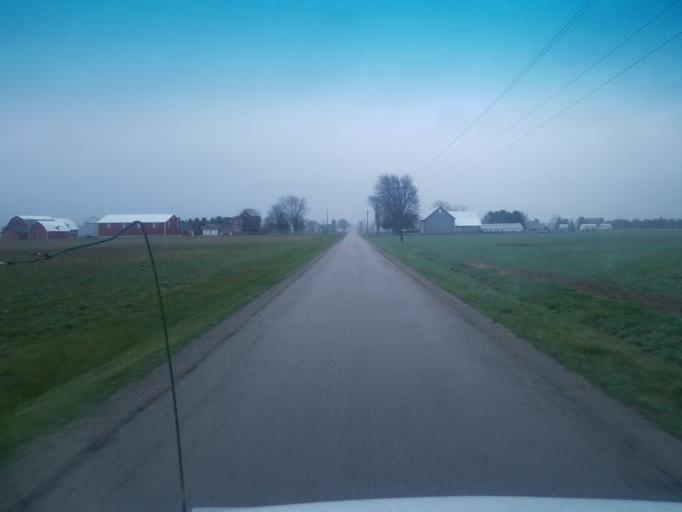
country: US
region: Ohio
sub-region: Fulton County
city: Archbold
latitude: 41.4238
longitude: -84.2477
